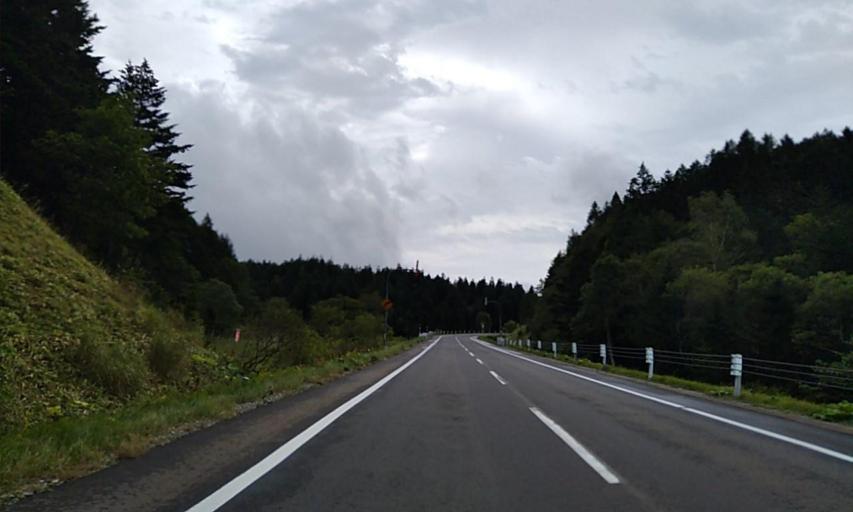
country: JP
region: Hokkaido
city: Abashiri
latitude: 43.6249
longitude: 144.5779
